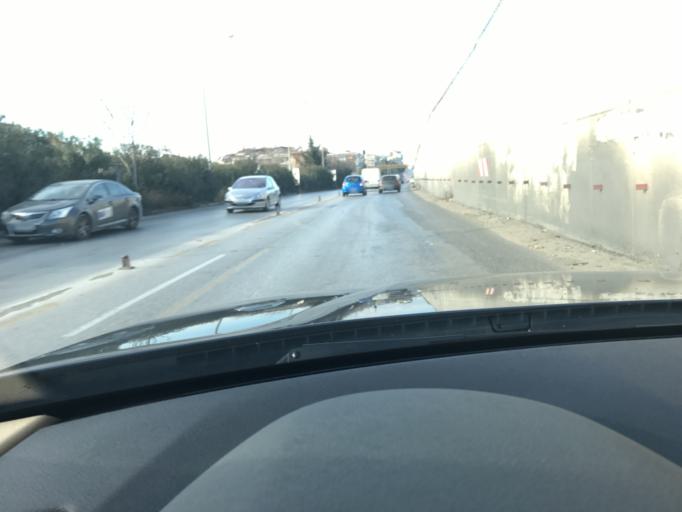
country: GR
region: Central Macedonia
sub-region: Nomos Thessalonikis
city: Stavroupoli
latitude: 40.6771
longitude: 22.9361
